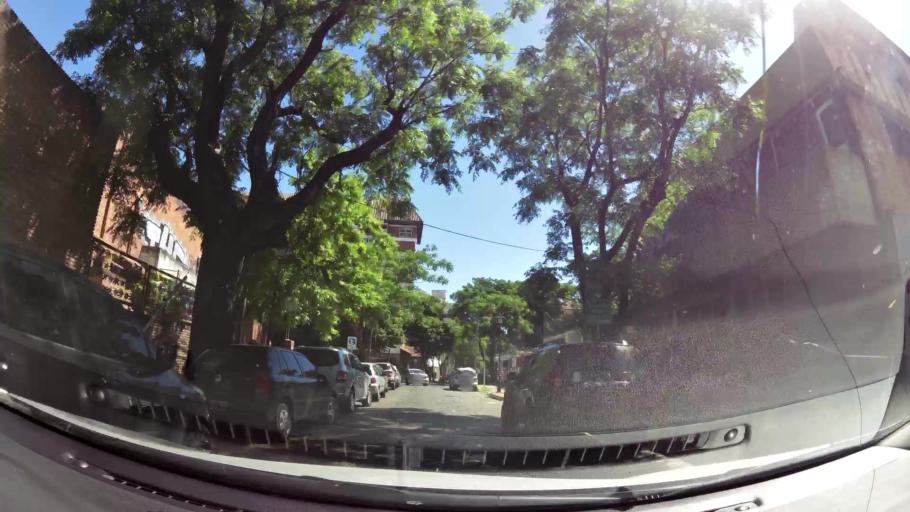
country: AR
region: Buenos Aires
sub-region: Partido de San Isidro
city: San Isidro
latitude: -34.4698
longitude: -58.5130
